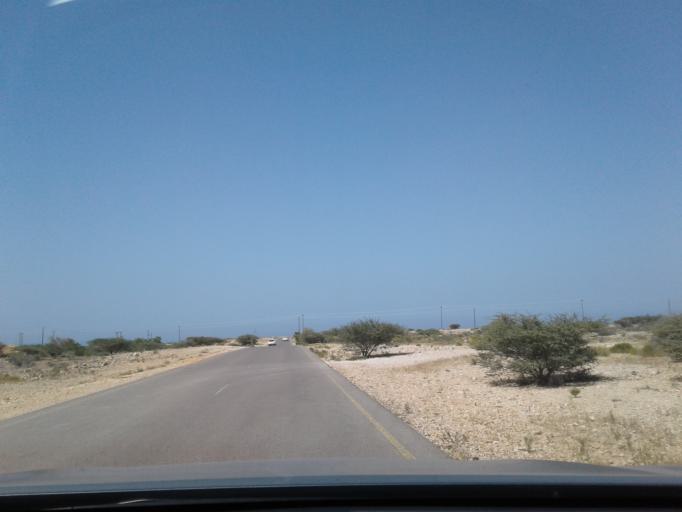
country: OM
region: Ash Sharqiyah
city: Al Qabil
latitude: 23.0384
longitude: 59.0711
